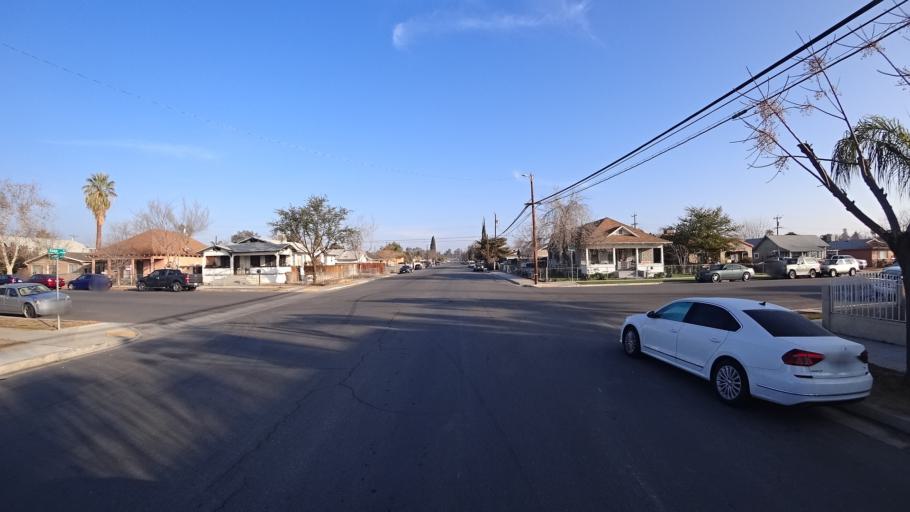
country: US
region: California
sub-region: Kern County
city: Bakersfield
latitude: 35.3814
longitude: -118.9845
